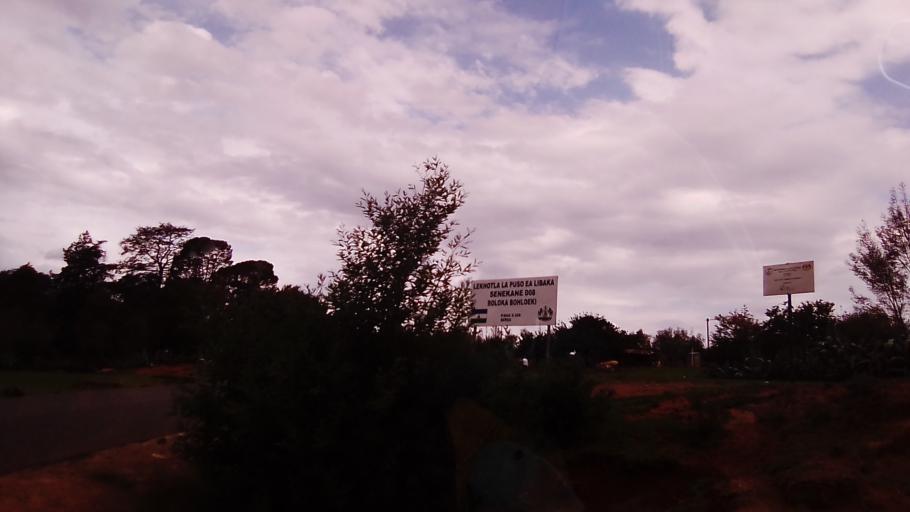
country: LS
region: Berea
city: Teyateyaneng
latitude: -29.3329
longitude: 27.7092
